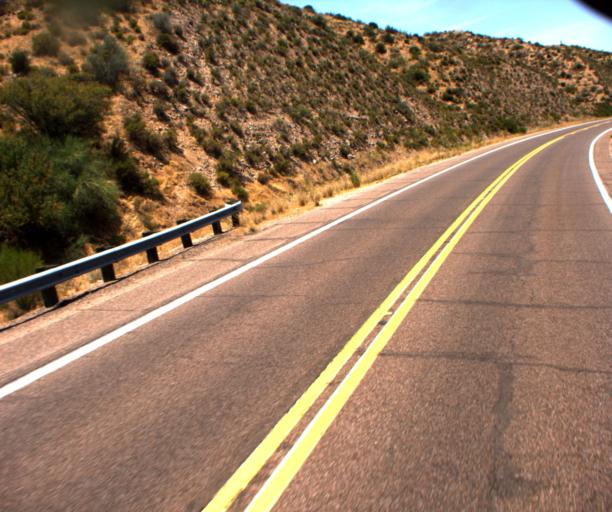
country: US
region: Arizona
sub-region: Gila County
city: Tonto Basin
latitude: 33.7573
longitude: -111.2507
